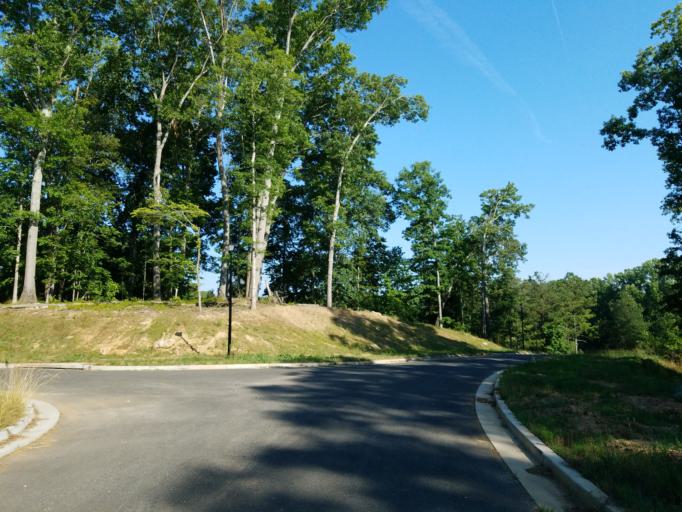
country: US
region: Georgia
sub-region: Fulton County
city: Milton
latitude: 34.1781
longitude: -84.3319
